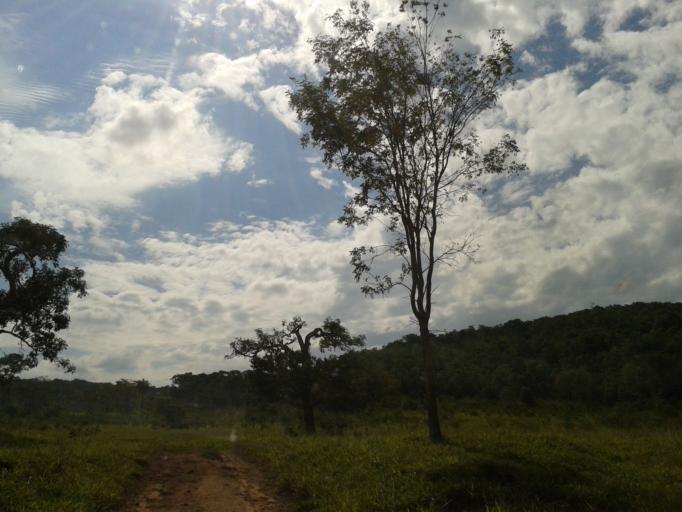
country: BR
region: Minas Gerais
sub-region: Campina Verde
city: Campina Verde
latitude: -19.3948
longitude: -49.6692
